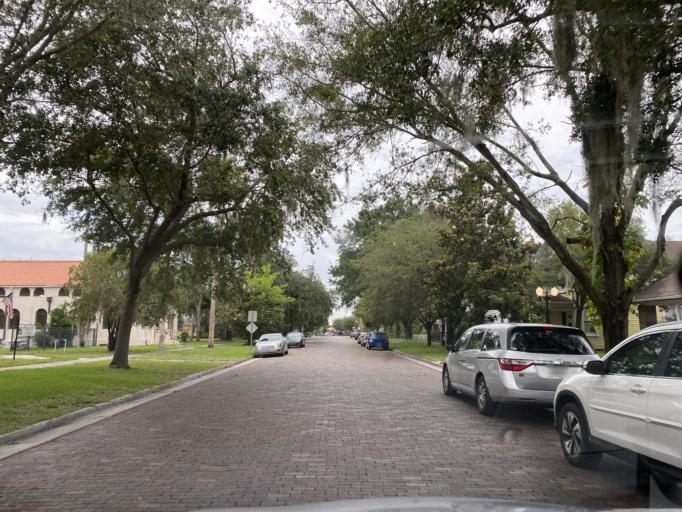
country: US
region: Florida
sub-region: Seminole County
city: Sanford
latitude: 28.8083
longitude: -81.2670
